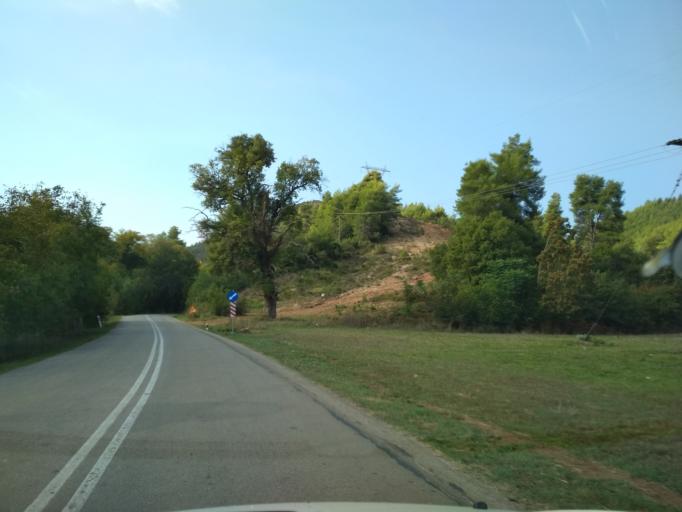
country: GR
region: Central Greece
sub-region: Nomos Evvoias
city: Mantoudi
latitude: 38.7799
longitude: 23.4701
